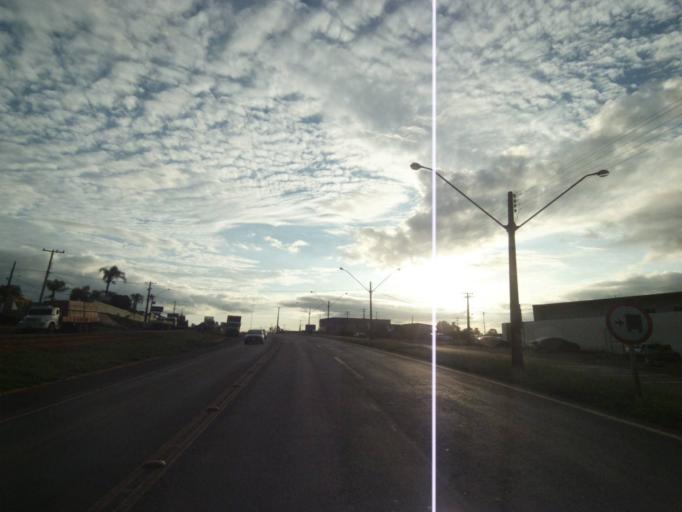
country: BR
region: Parana
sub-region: Telemaco Borba
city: Telemaco Borba
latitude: -24.3309
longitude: -50.6470
